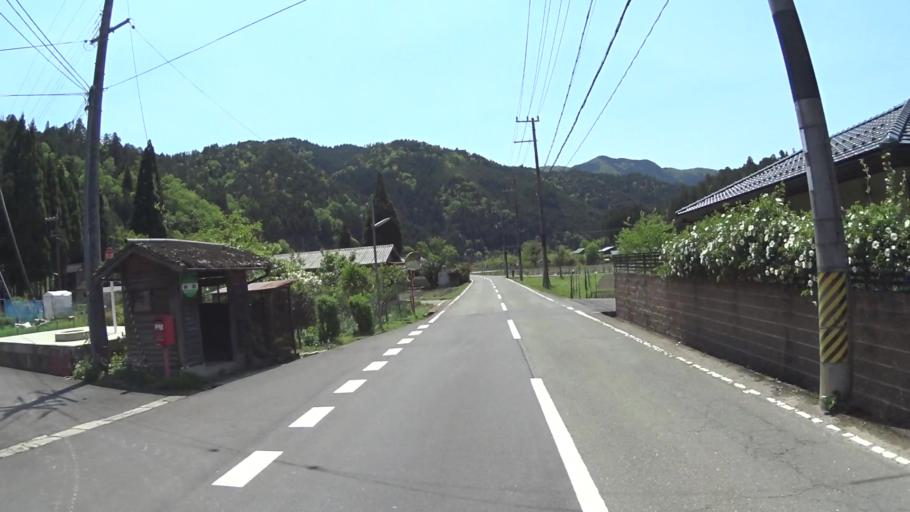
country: JP
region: Kyoto
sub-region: Kyoto-shi
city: Kamigyo-ku
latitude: 35.2015
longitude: 135.6821
